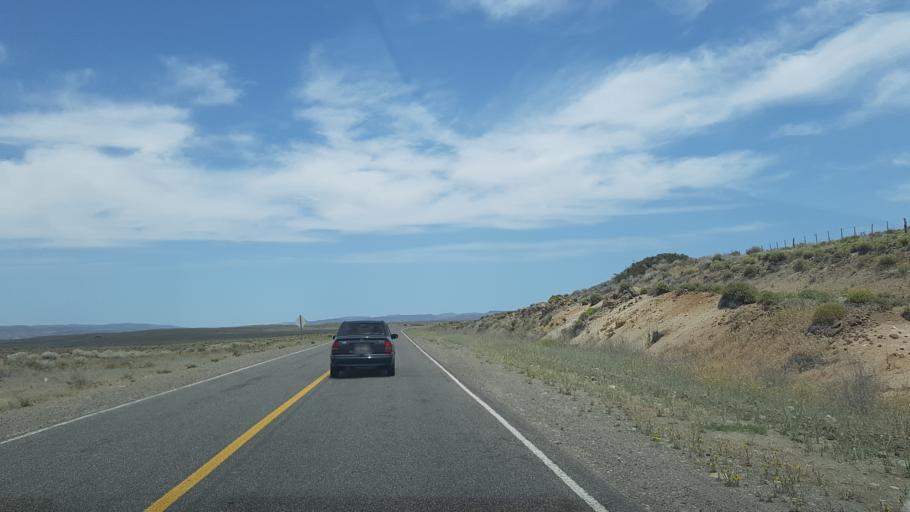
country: AR
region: Rio Negro
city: Pilcaniyeu
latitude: -40.5091
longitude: -70.6858
